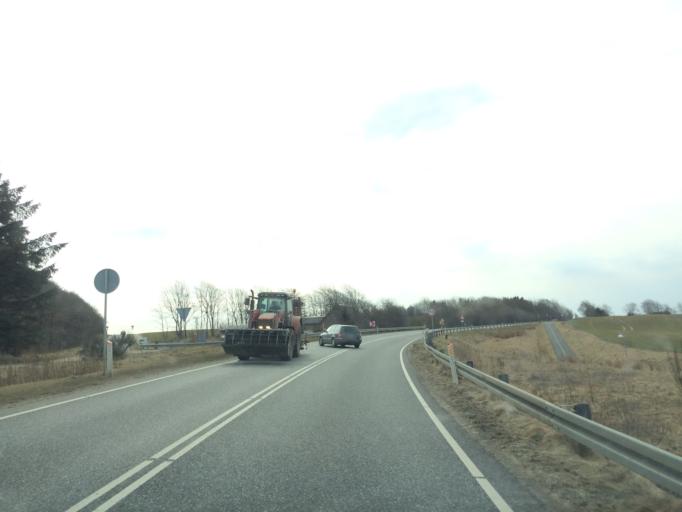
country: DK
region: Central Jutland
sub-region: Ringkobing-Skjern Kommune
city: Videbaek
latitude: 56.1075
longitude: 8.5072
